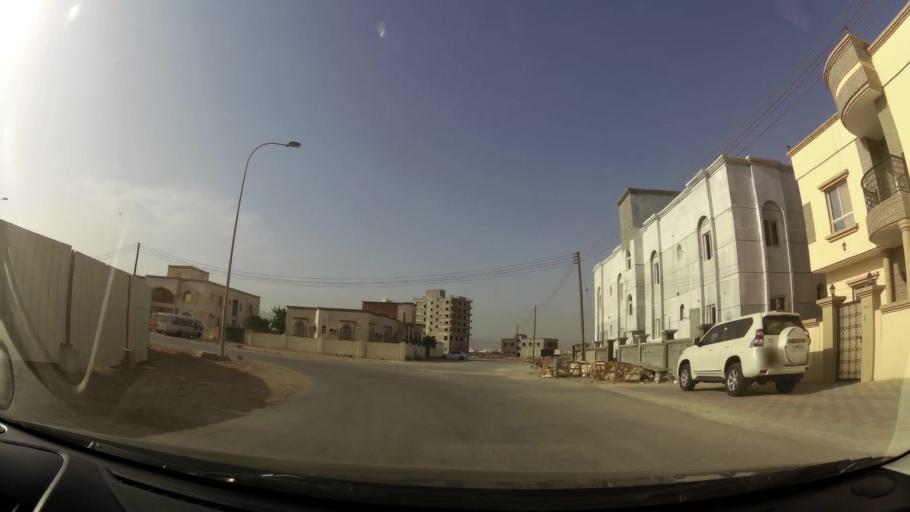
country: OM
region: Zufar
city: Salalah
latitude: 17.0238
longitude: 54.0226
